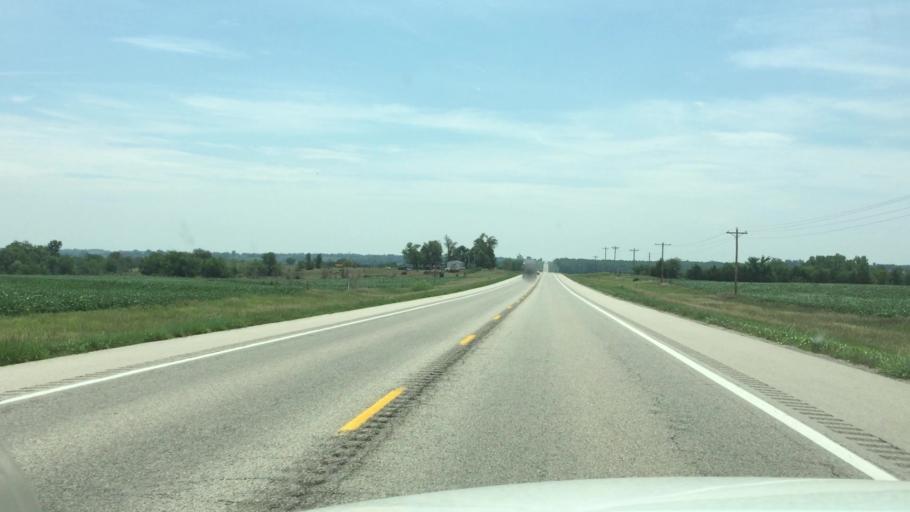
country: US
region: Kansas
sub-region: Jackson County
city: Holton
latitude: 39.6487
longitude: -95.7309
